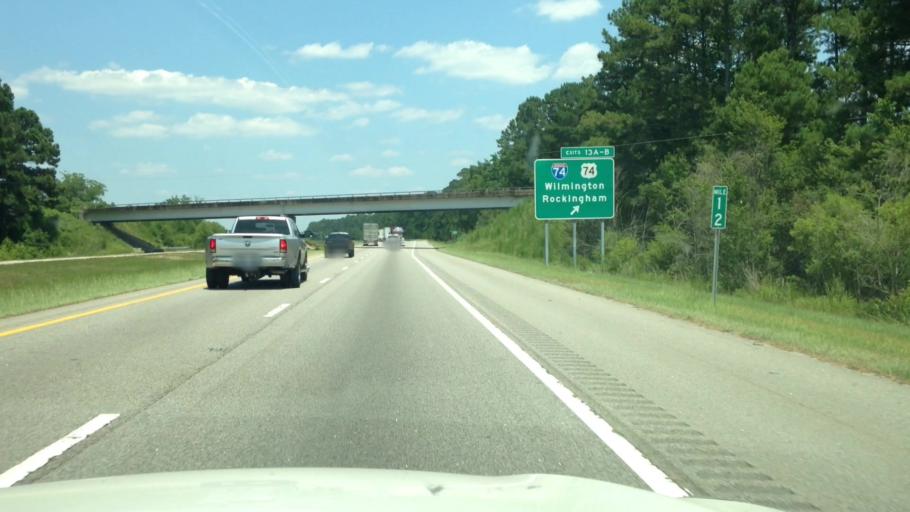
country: US
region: North Carolina
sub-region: Robeson County
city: Fairmont
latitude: 34.5871
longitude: -79.1277
